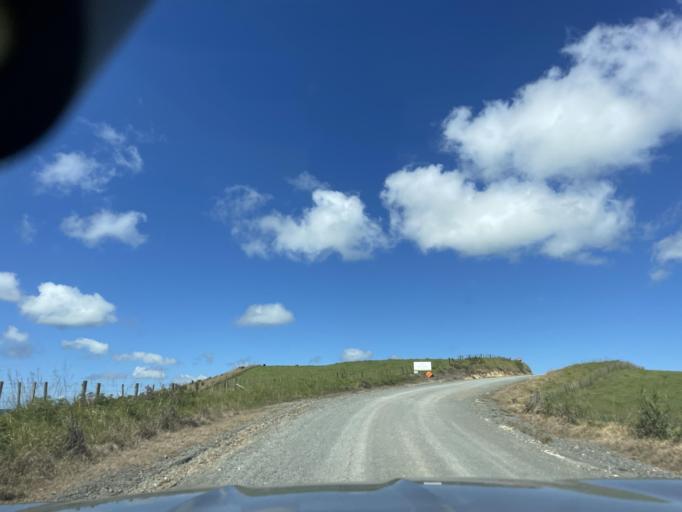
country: NZ
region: Auckland
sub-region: Auckland
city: Wellsford
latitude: -36.2753
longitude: 174.3703
